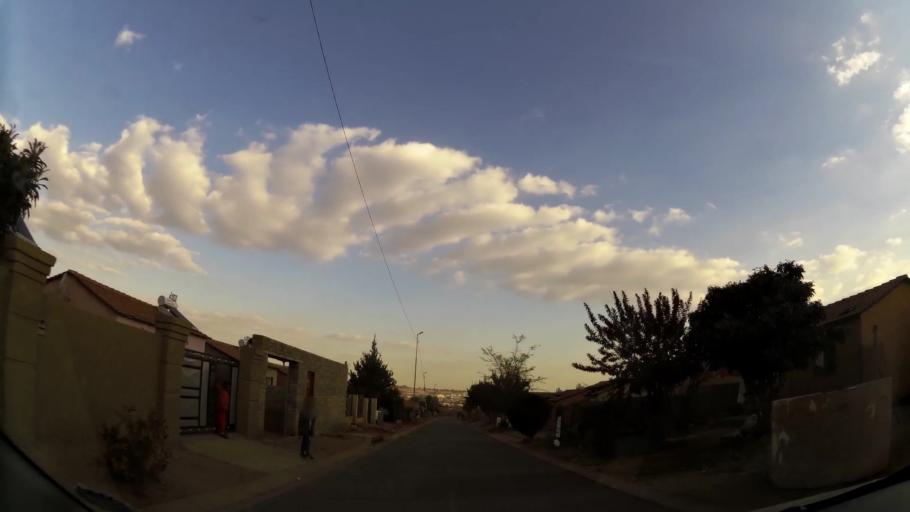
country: ZA
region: Gauteng
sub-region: West Rand District Municipality
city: Krugersdorp
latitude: -26.0774
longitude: 27.7599
